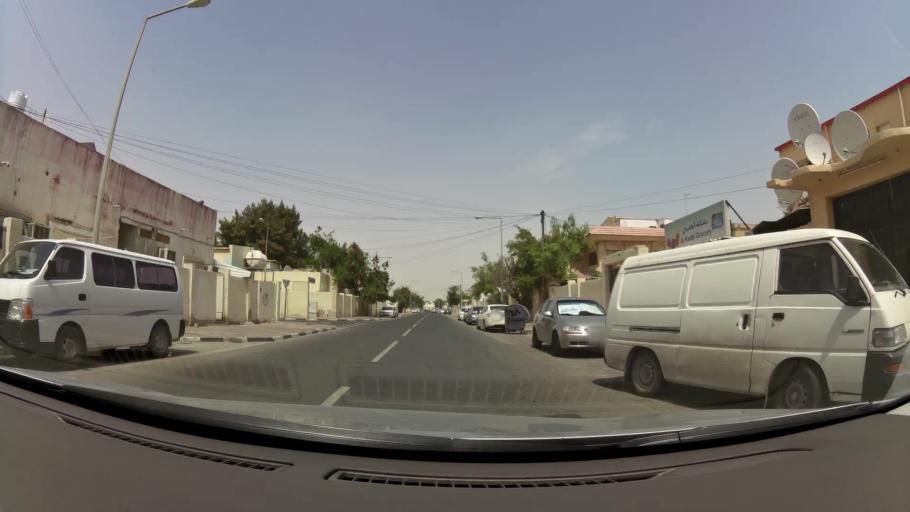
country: QA
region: Baladiyat ad Dawhah
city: Doha
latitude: 25.3166
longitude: 51.4809
